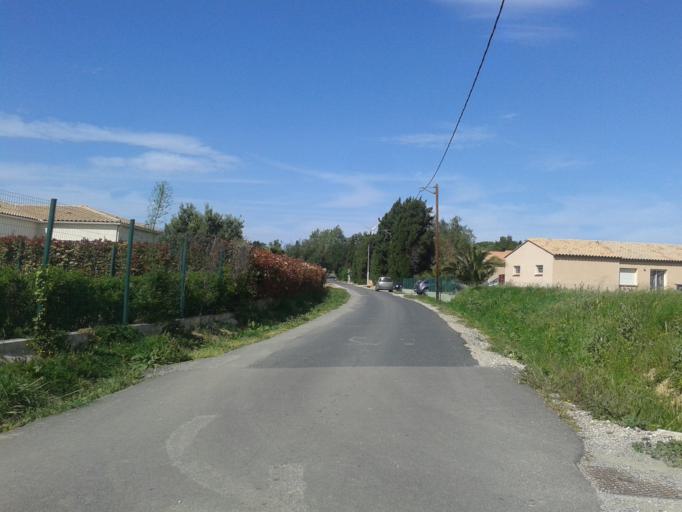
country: FR
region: Languedoc-Roussillon
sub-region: Departement des Pyrenees-Orientales
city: Corneilla-la-Riviere
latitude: 42.6988
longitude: 2.7337
